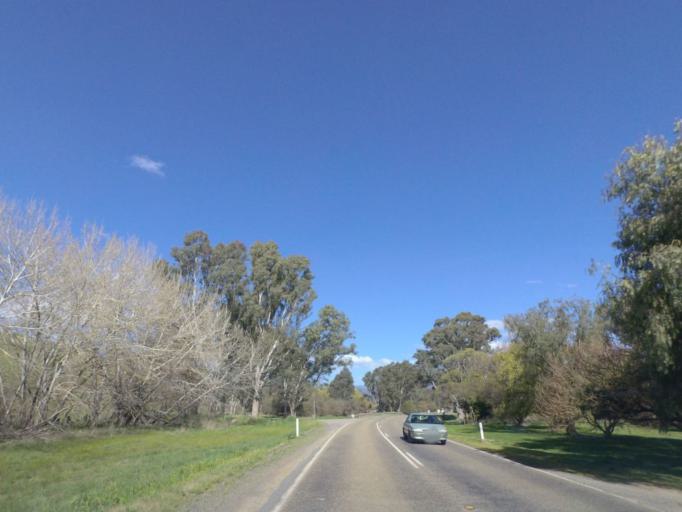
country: AU
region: Victoria
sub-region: Murrindindi
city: Alexandra
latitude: -37.2334
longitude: 145.7682
